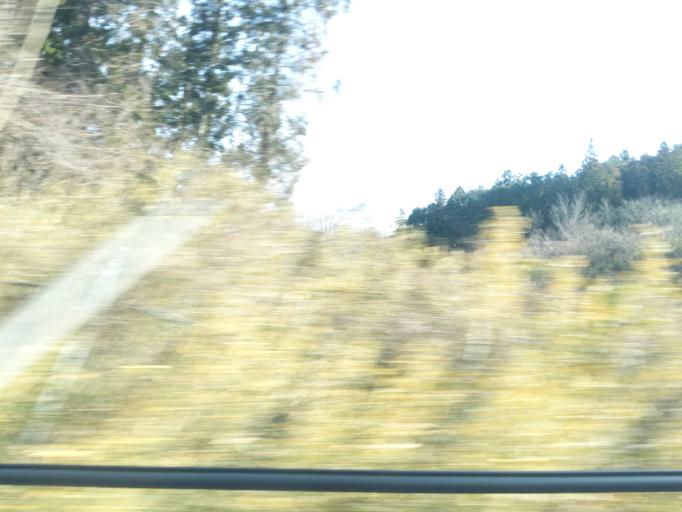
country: JP
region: Miyagi
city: Tomiya
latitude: 38.4153
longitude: 140.9638
